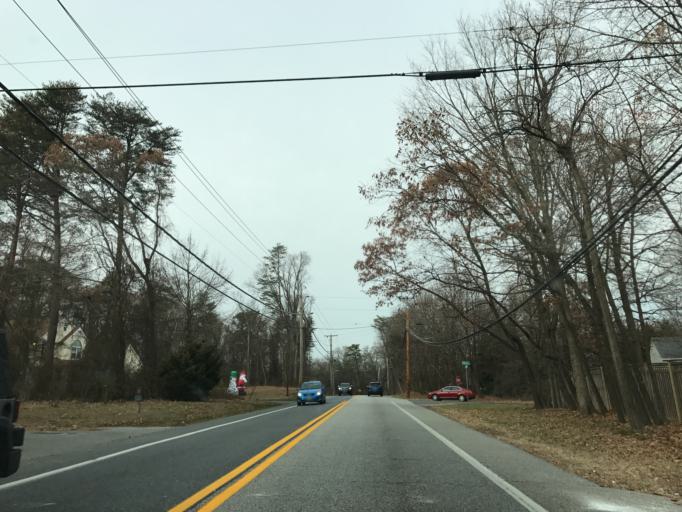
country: US
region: Maryland
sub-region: Anne Arundel County
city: Pasadena
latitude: 39.1001
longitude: -76.5500
